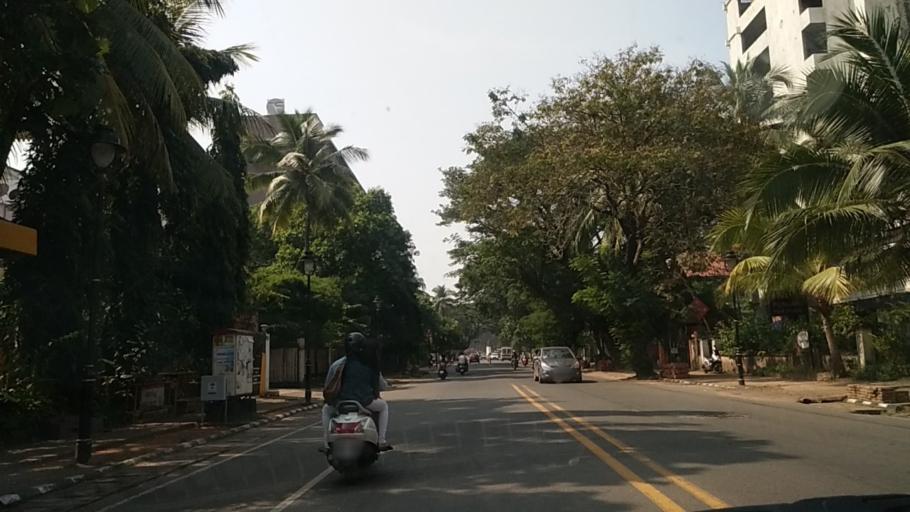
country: IN
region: Goa
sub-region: North Goa
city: Panaji
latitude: 15.4853
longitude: 73.8109
